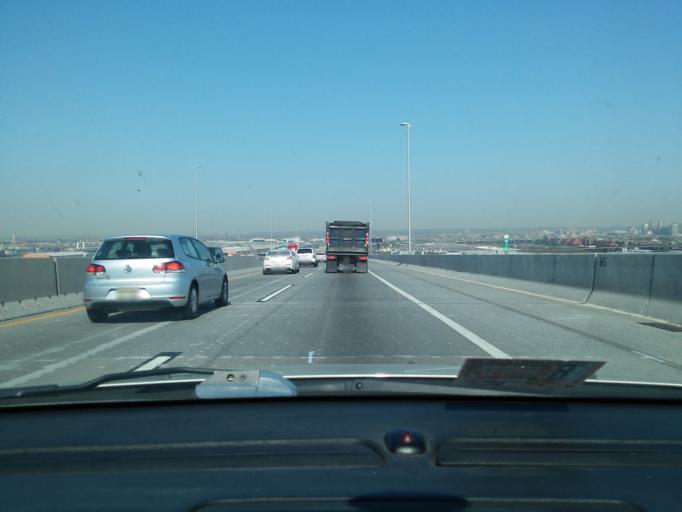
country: US
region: New Jersey
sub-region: Hudson County
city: Bayonne
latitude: 40.6974
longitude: -74.1252
